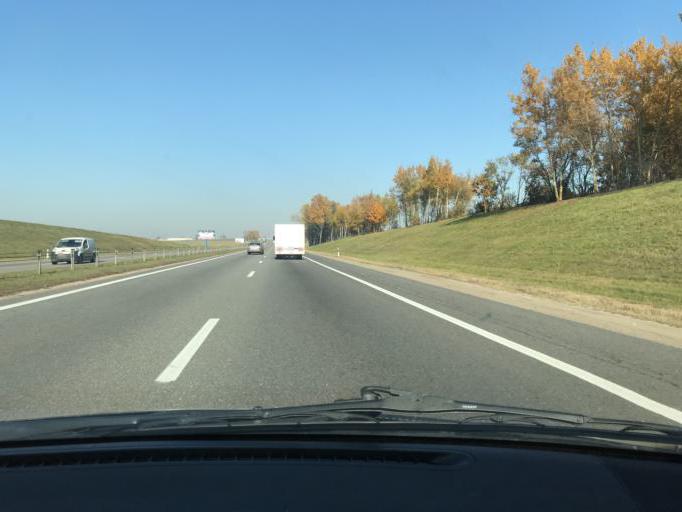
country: BY
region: Minsk
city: Samakhvalavichy
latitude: 53.7743
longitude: 27.5237
